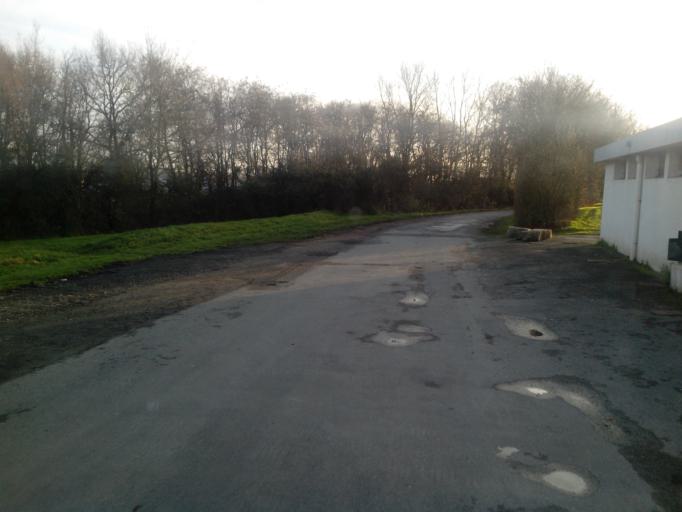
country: FR
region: Pays de la Loire
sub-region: Departement de Maine-et-Loire
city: Cholet
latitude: 47.0605
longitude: -0.9066
